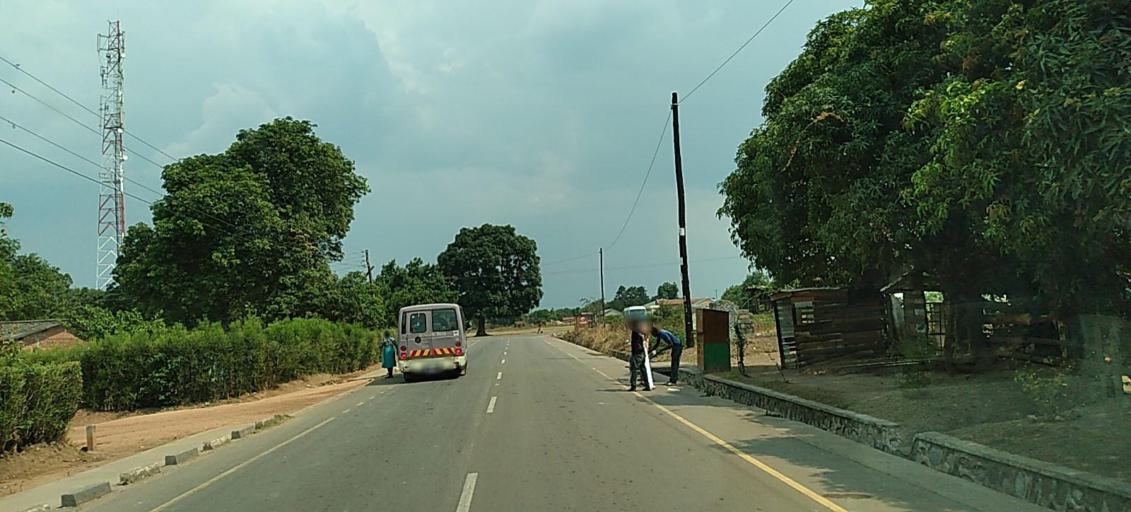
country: ZM
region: Copperbelt
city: Kalulushi
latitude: -12.8505
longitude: 28.1342
